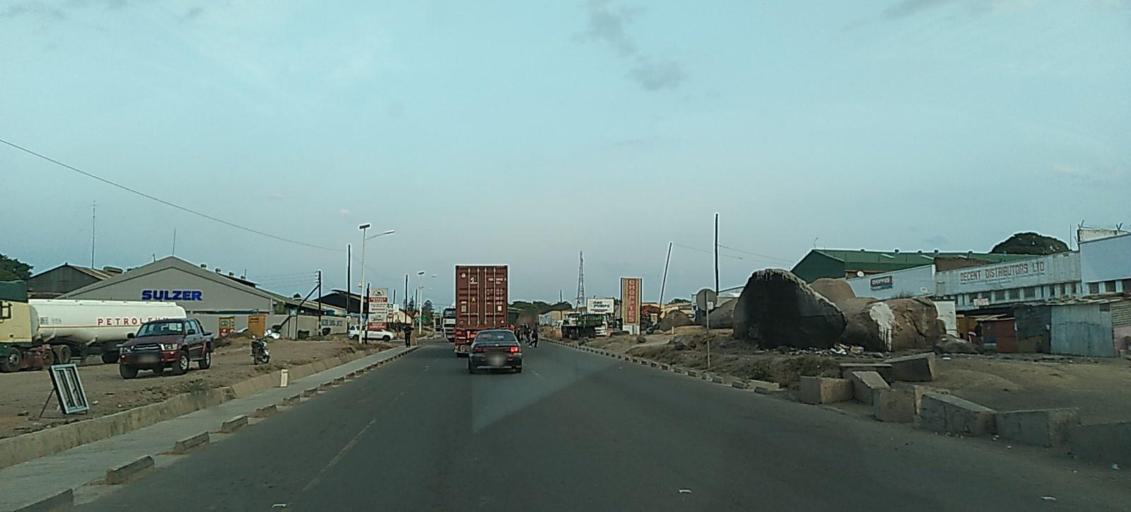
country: ZM
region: Copperbelt
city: Chingola
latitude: -12.5454
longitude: 27.8514
